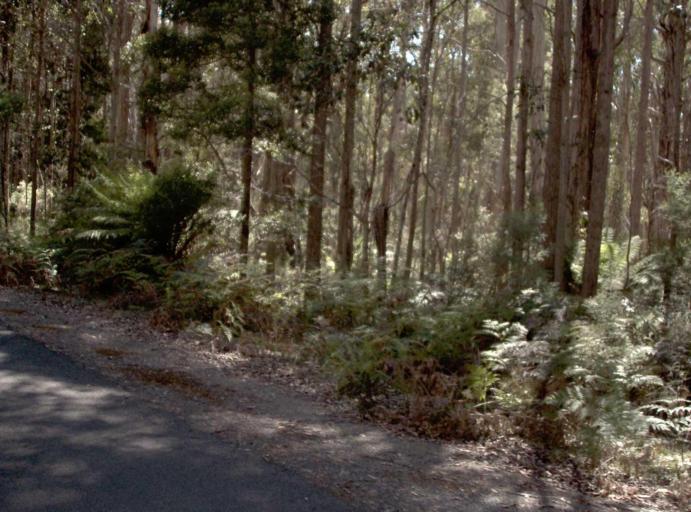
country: AU
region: New South Wales
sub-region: Bombala
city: Bombala
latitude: -37.0746
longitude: 148.7802
